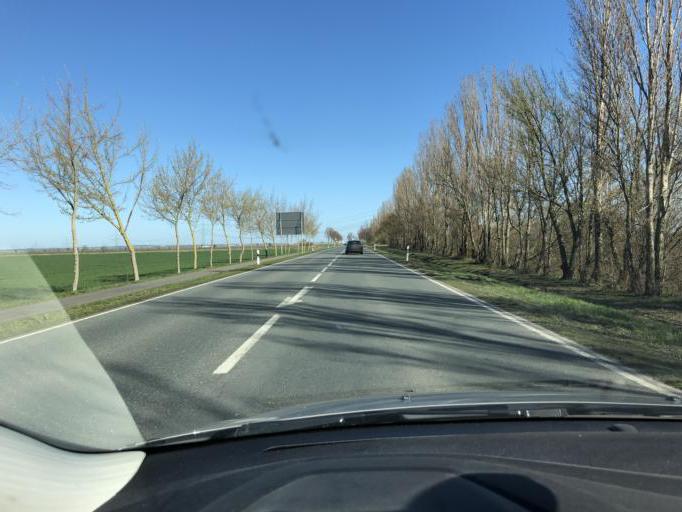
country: DE
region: Saxony-Anhalt
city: Welsleben
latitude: 52.0035
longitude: 11.6054
